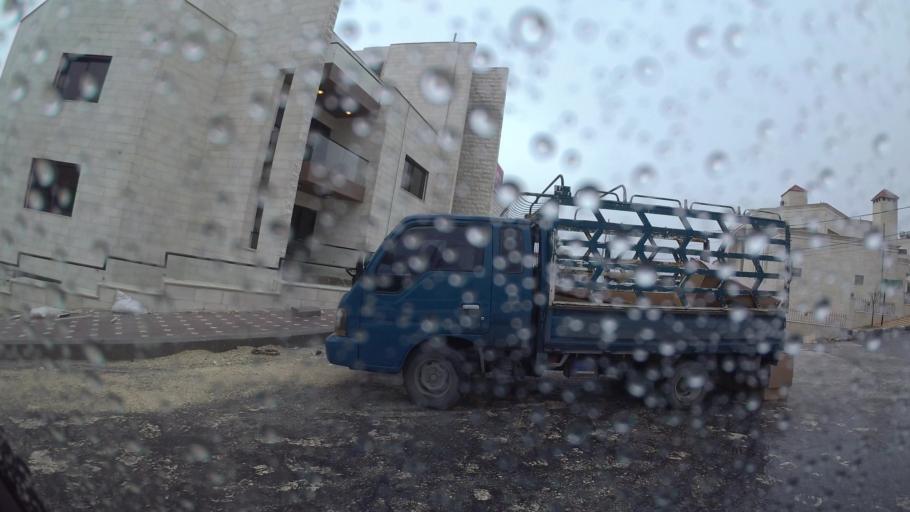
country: JO
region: Amman
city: Al Jubayhah
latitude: 32.0099
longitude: 35.8305
